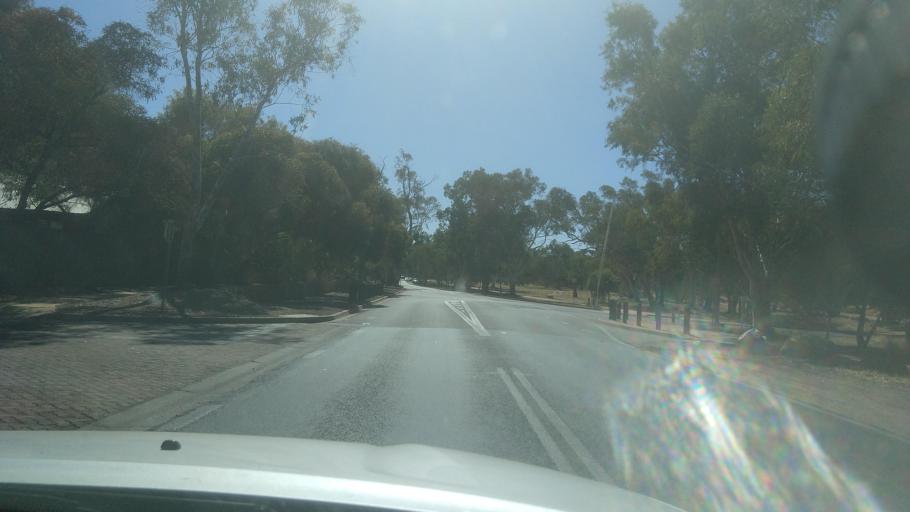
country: AU
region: Northern Territory
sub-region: Alice Springs
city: Alice Springs
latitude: -23.7208
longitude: 133.8734
